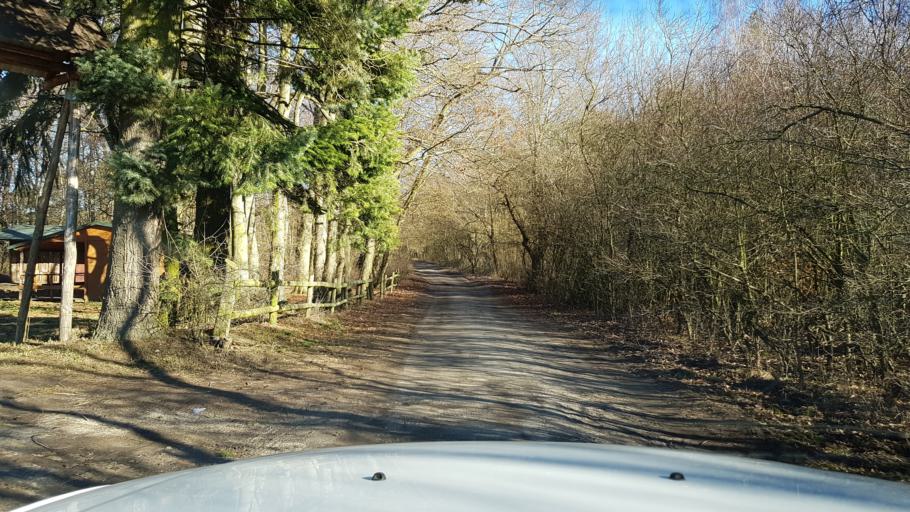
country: PL
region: West Pomeranian Voivodeship
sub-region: Powiat pyrzycki
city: Lipiany
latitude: 53.0253
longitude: 15.0133
